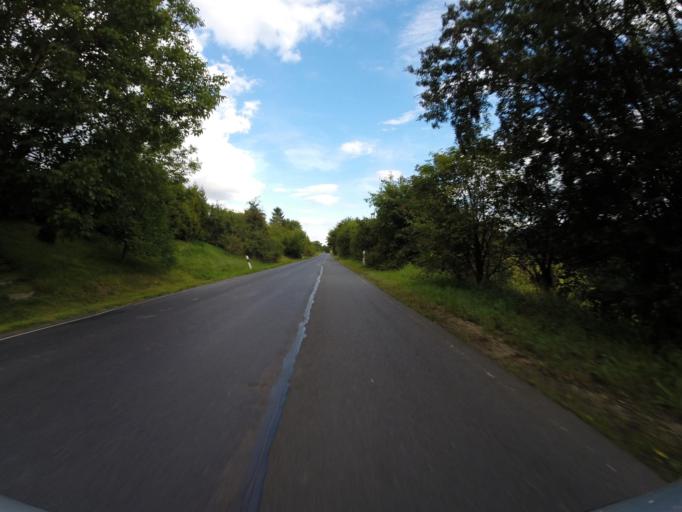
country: DE
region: Thuringia
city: Oettern
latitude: 50.9573
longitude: 11.3602
